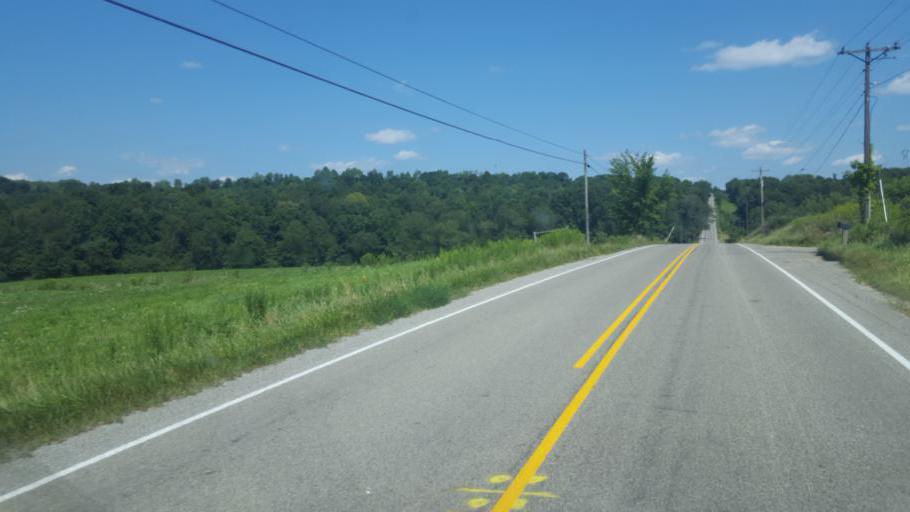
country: US
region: Pennsylvania
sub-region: Clarion County
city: Knox
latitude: 41.1037
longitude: -79.6460
